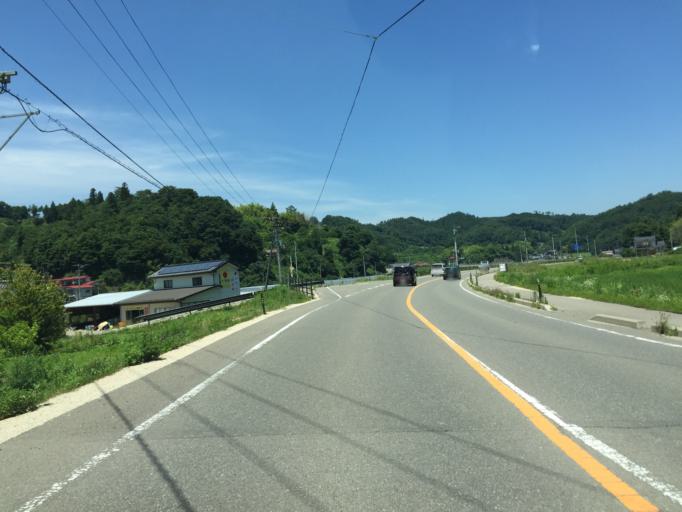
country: JP
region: Fukushima
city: Hobaramachi
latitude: 37.7689
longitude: 140.6107
